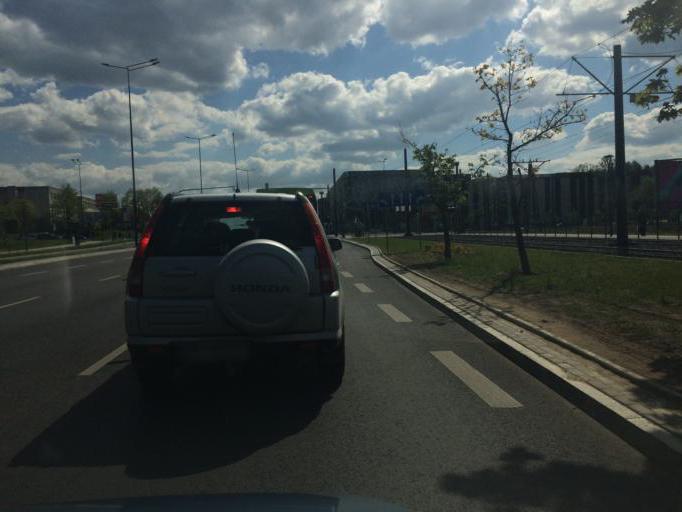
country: PL
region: Warmian-Masurian Voivodeship
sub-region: Powiat olsztynski
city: Olsztyn
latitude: 53.7569
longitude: 20.4864
